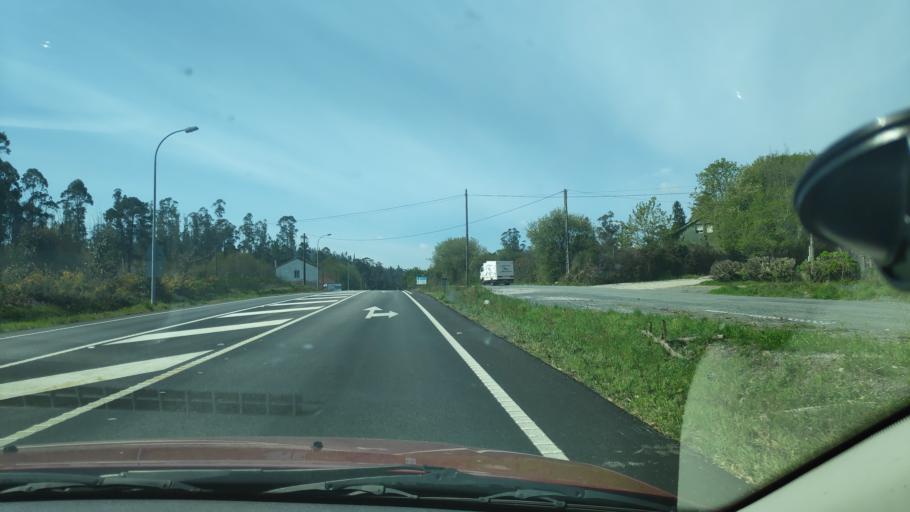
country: ES
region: Galicia
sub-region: Provincia da Coruna
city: Ames
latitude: 42.8794
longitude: -8.6773
